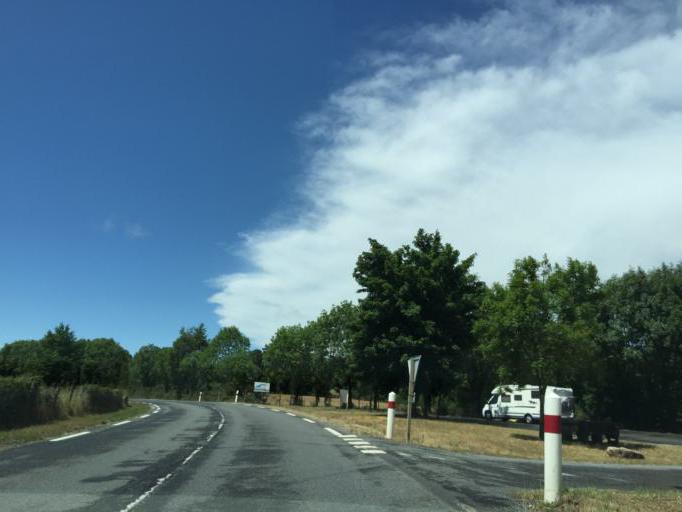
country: FR
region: Midi-Pyrenees
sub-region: Departement de l'Aveyron
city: Severac-le-Chateau
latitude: 44.2251
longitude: 2.9933
